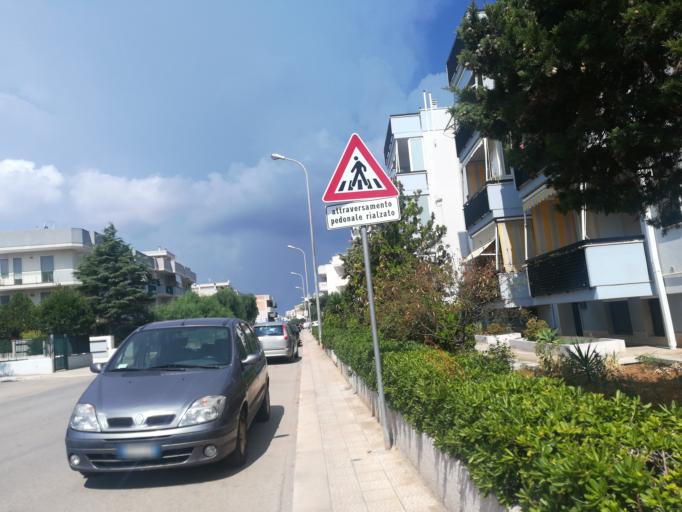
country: IT
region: Apulia
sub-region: Provincia di Bari
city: Polignano a Mare
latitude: 40.9886
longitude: 17.2260
